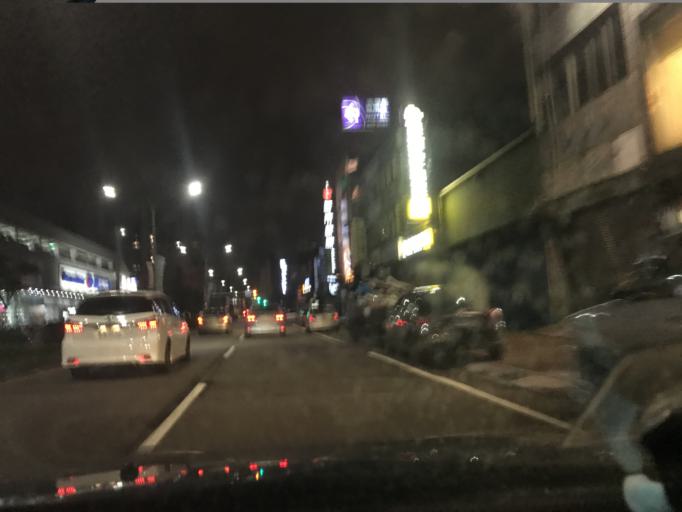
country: TW
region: Taiwan
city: Taoyuan City
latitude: 24.9632
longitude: 121.2328
